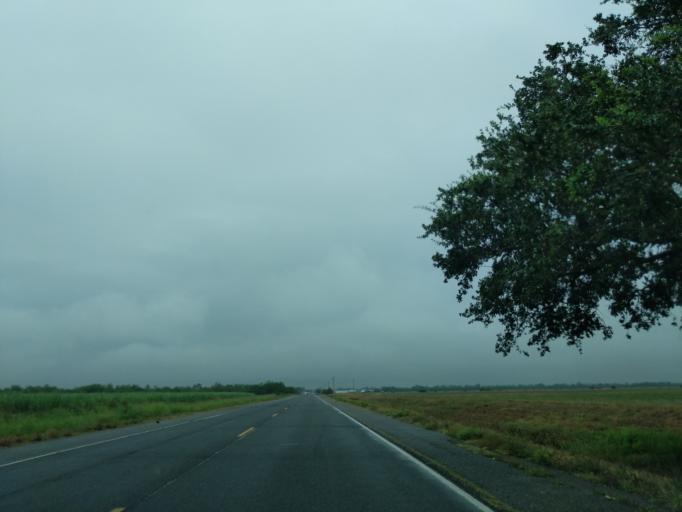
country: US
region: Louisiana
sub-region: Vermilion Parish
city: Kaplan
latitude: 29.9915
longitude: -92.2481
